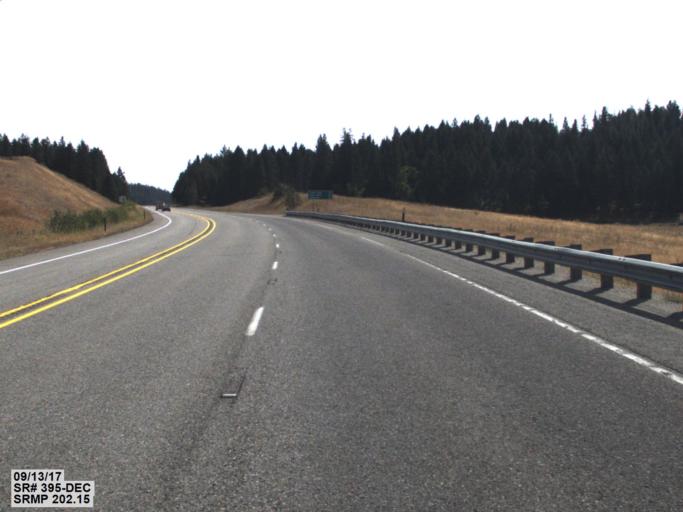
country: US
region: Washington
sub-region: Stevens County
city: Chewelah
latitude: 48.2043
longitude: -117.7142
